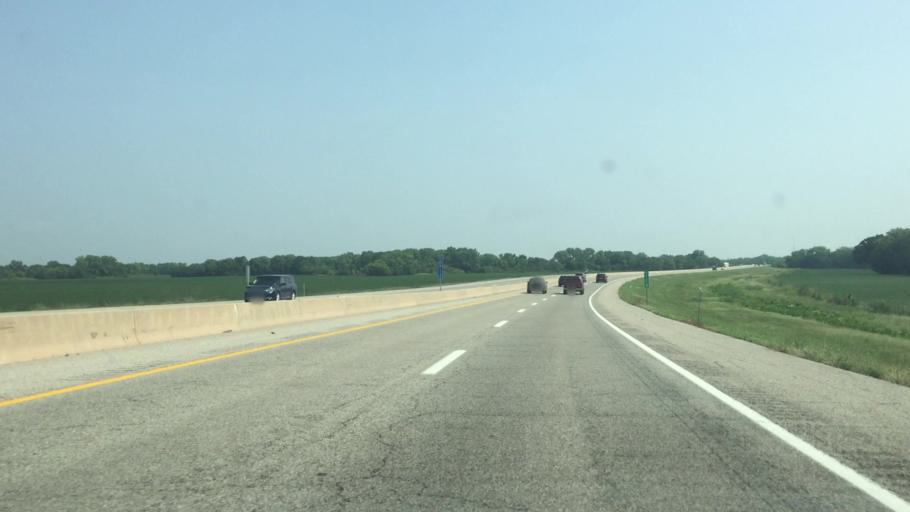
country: US
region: Kansas
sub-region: Lyon County
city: Emporia
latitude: 38.3787
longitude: -96.2665
